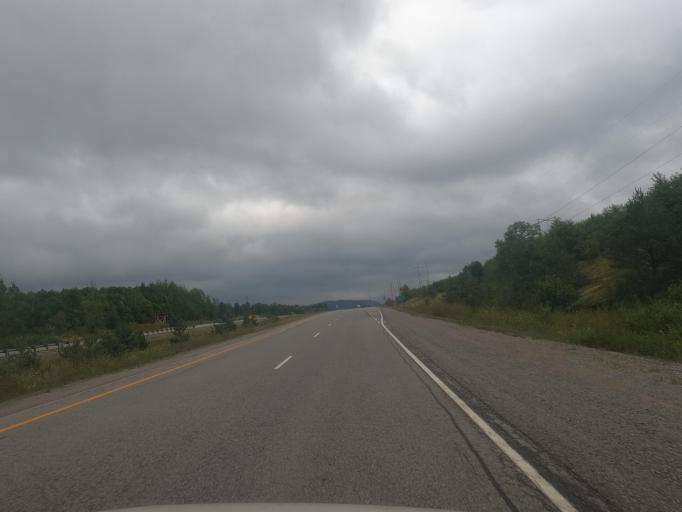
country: CA
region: Ontario
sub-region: Algoma
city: Sault Ste. Marie
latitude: 46.5577
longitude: -84.2144
